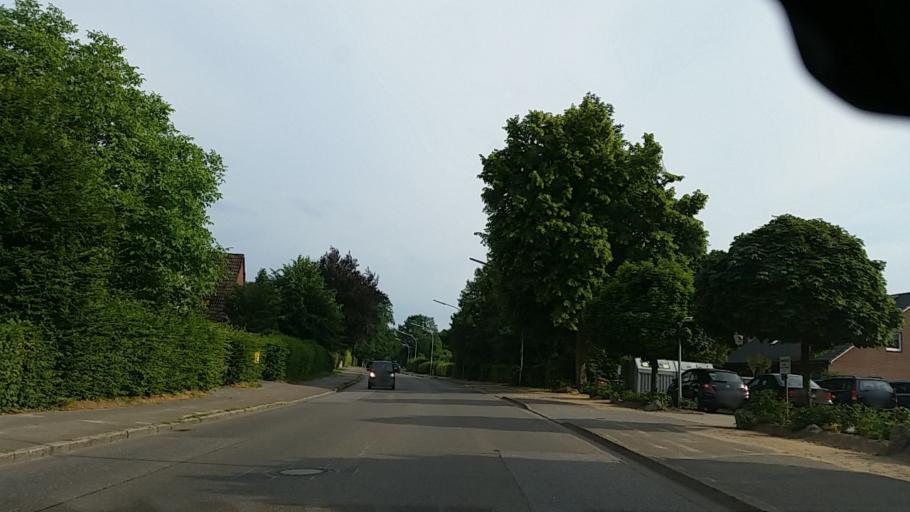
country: DE
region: Schleswig-Holstein
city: Halstenbek
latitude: 53.5944
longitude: 9.8224
